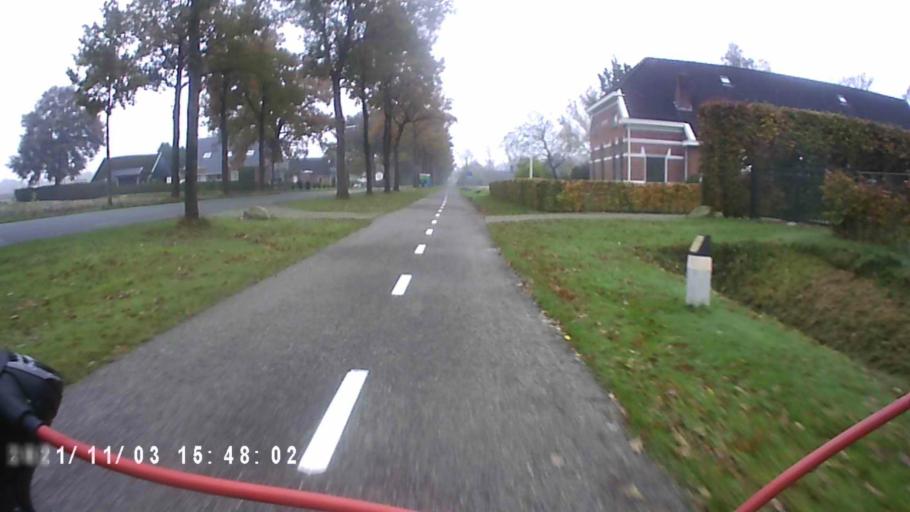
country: NL
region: Groningen
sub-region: Gemeente Leek
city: Leek
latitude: 53.0887
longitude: 6.3395
